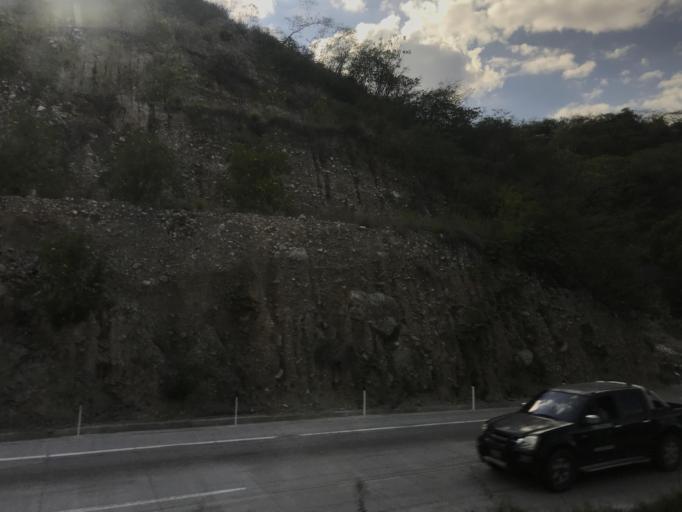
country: GT
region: El Progreso
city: Guastatoya
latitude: 14.8490
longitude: -90.1042
